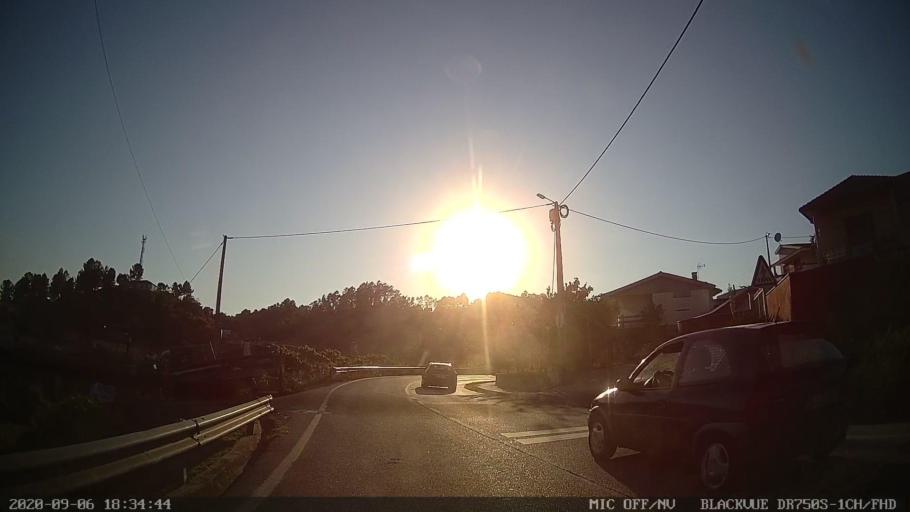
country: PT
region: Porto
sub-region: Amarante
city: Amarante
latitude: 41.2557
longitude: -8.0525
